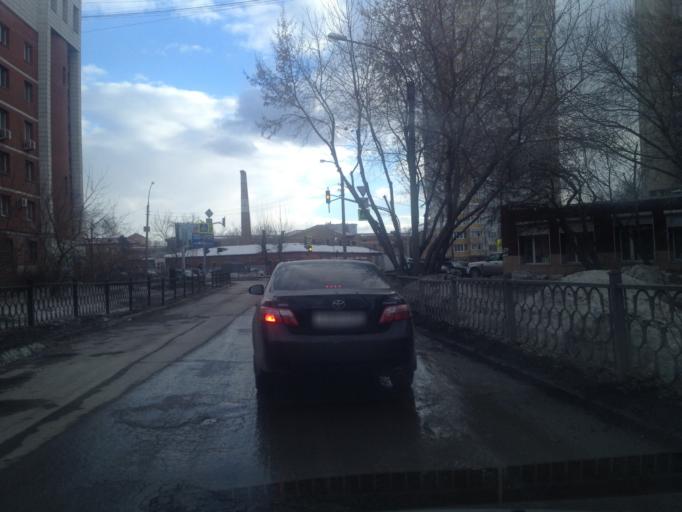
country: RU
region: Sverdlovsk
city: Yekaterinburg
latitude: 56.8540
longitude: 60.5821
